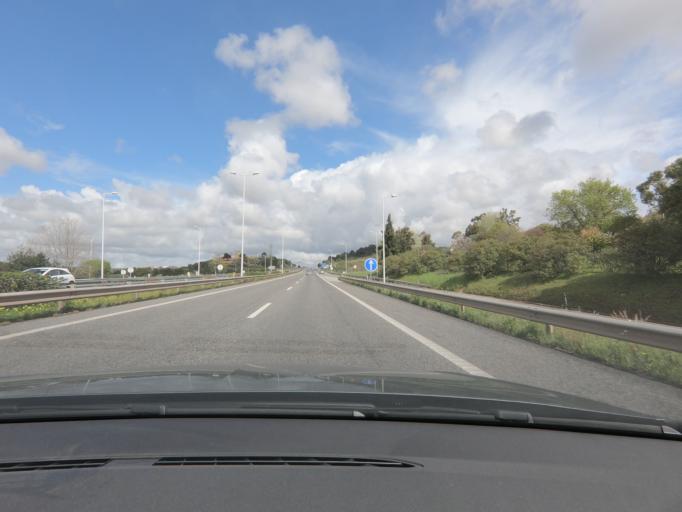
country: PT
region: Lisbon
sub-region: Oeiras
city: Quejas
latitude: 38.7167
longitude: -9.2689
